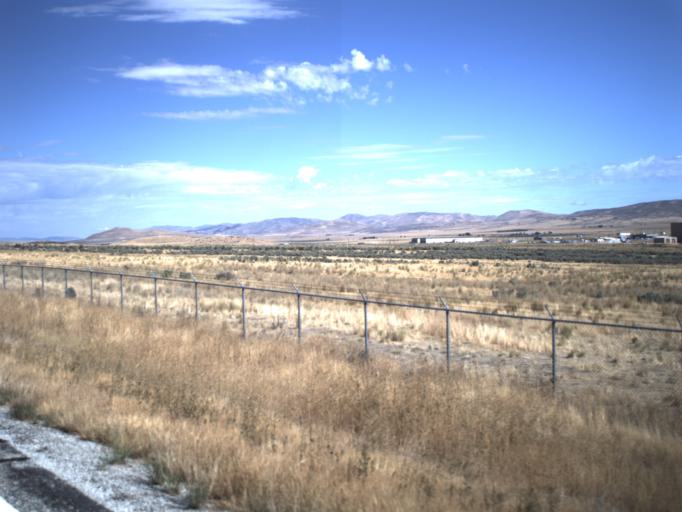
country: US
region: Utah
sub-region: Box Elder County
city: Tremonton
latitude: 41.7050
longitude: -112.4495
